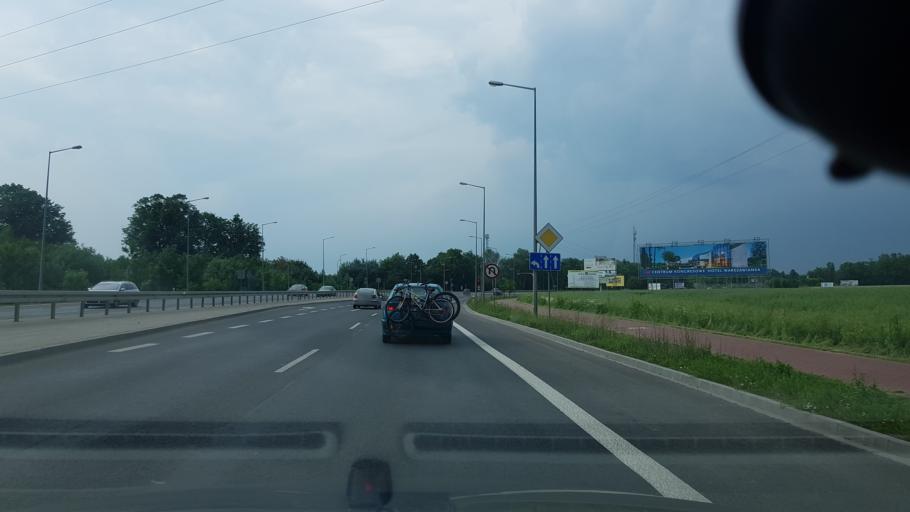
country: PL
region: Masovian Voivodeship
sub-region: Powiat legionowski
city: Bialobrzegi
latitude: 52.4701
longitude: 21.0294
